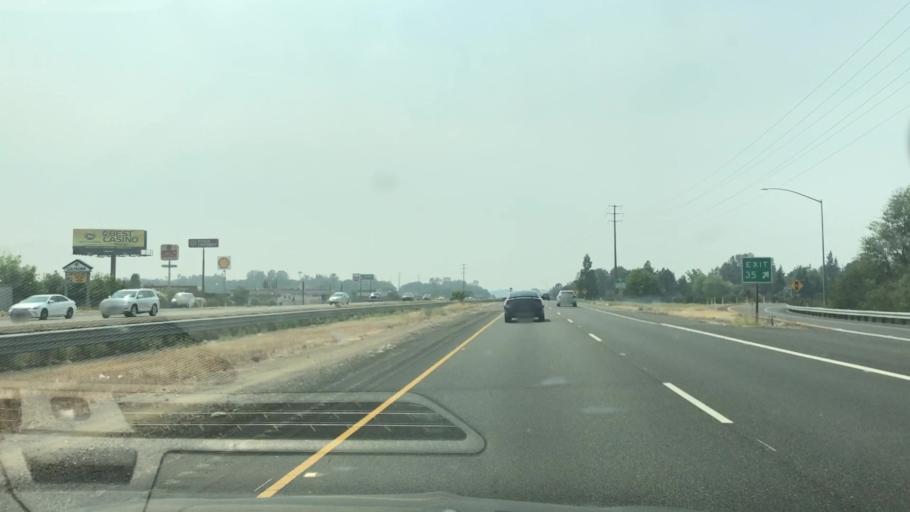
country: US
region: California
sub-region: El Dorado County
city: Cameron Park
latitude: 38.6596
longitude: -120.9657
